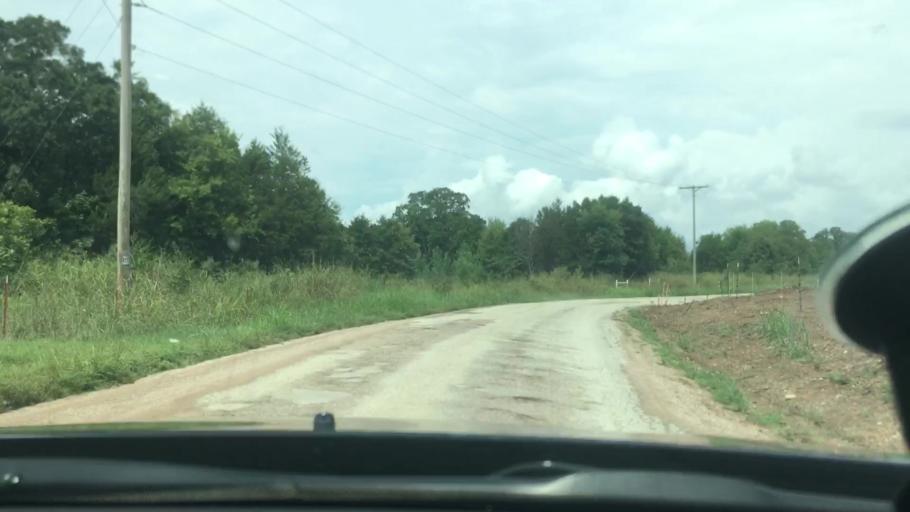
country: US
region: Oklahoma
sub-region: Carter County
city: Dickson
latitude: 34.2414
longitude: -96.9166
